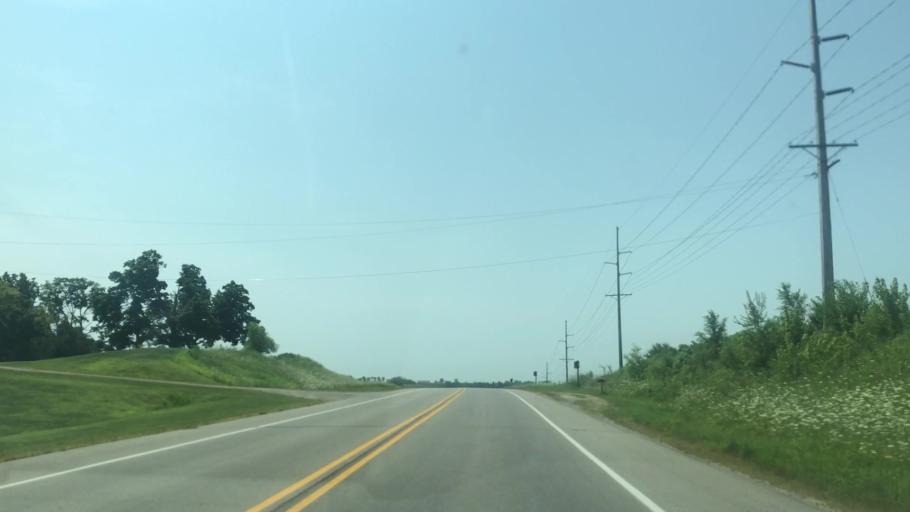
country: US
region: Iowa
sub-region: Marshall County
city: Marshalltown
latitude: 42.0265
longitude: -92.9604
